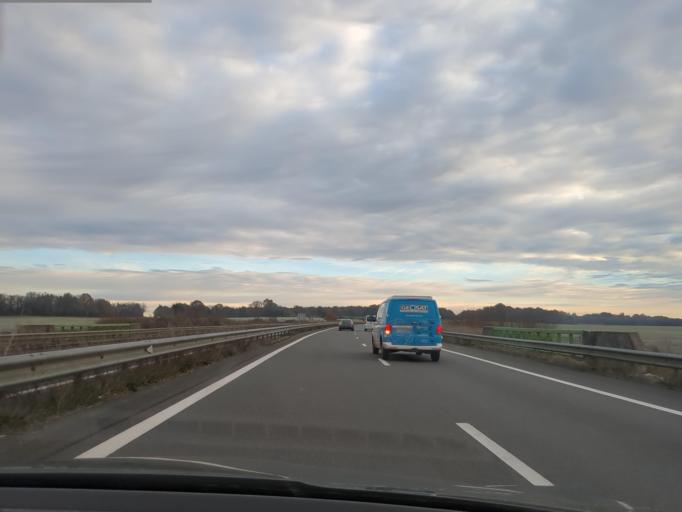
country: FR
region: Poitou-Charentes
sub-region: Departement de la Charente
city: Taponnat-Fleurignac
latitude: 45.7894
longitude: 0.4175
